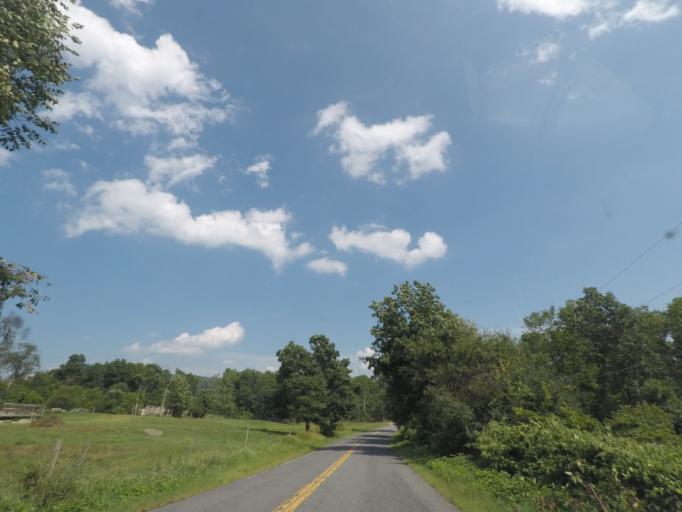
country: US
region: New York
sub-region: Saratoga County
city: Waterford
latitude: 42.8057
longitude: -73.5754
